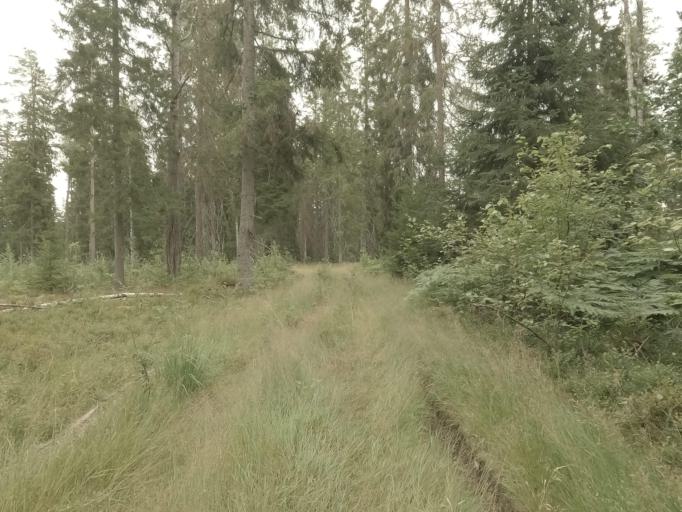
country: RU
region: Leningrad
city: Kamennogorsk
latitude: 61.0493
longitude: 29.1838
